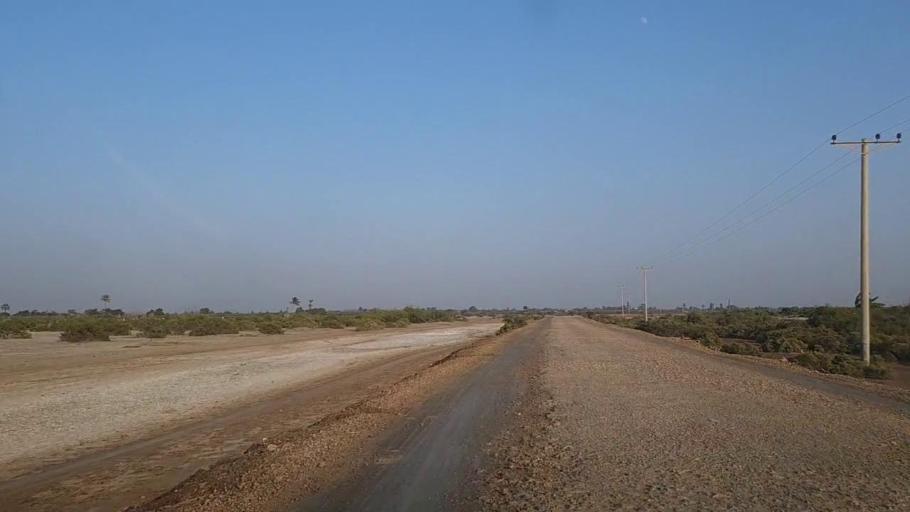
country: PK
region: Sindh
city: Keti Bandar
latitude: 24.2792
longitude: 67.6396
